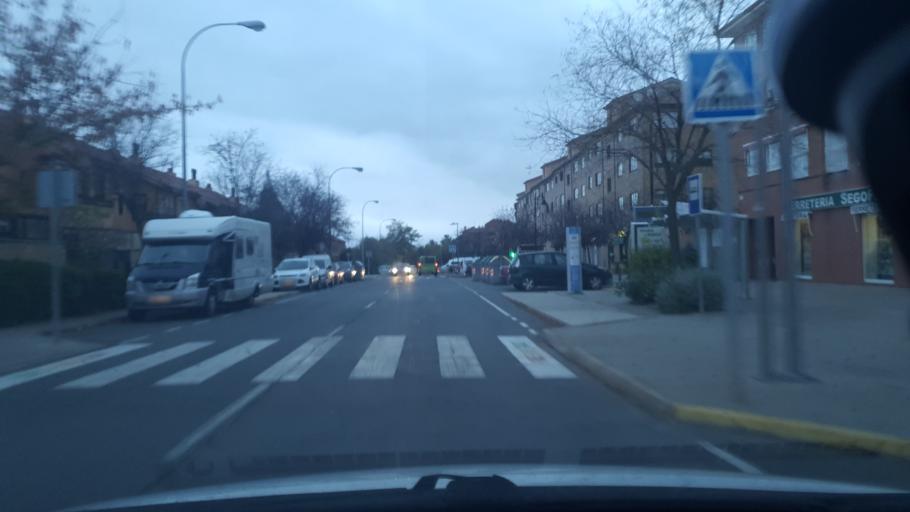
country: ES
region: Castille and Leon
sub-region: Provincia de Segovia
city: Segovia
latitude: 40.9294
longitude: -4.1009
